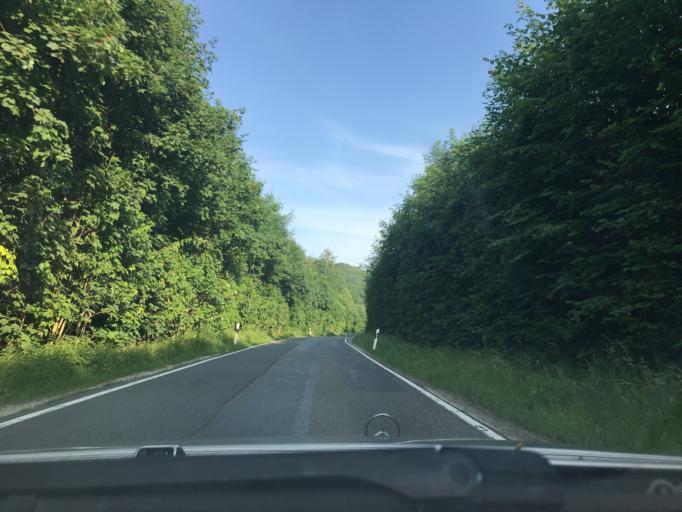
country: DE
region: Thuringia
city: Kleinbartloff
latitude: 51.3438
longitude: 10.3658
